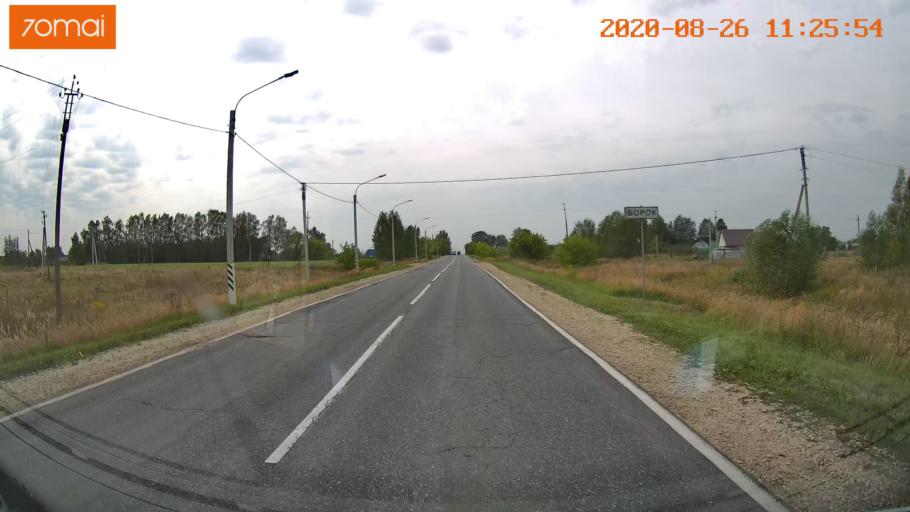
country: RU
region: Rjazan
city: Shilovo
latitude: 54.3378
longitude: 40.9563
